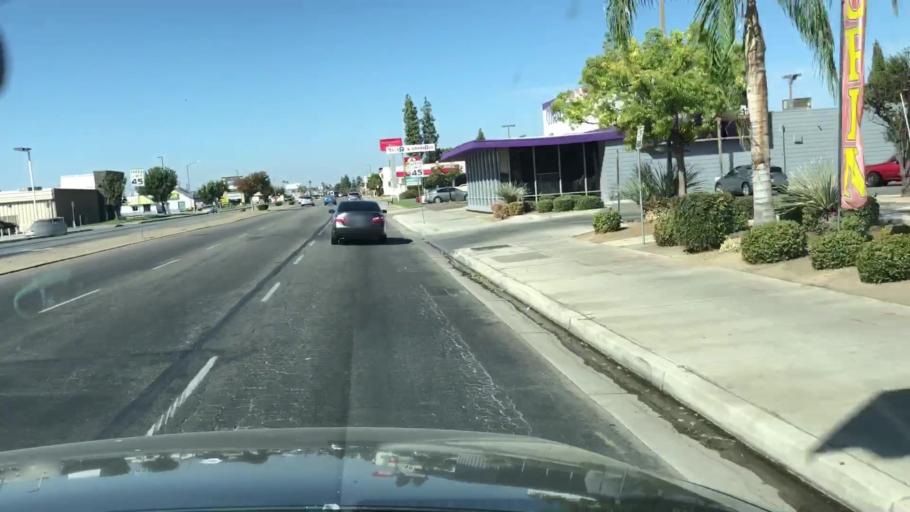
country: US
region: California
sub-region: Kern County
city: Bakersfield
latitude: 35.3396
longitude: -119.0437
